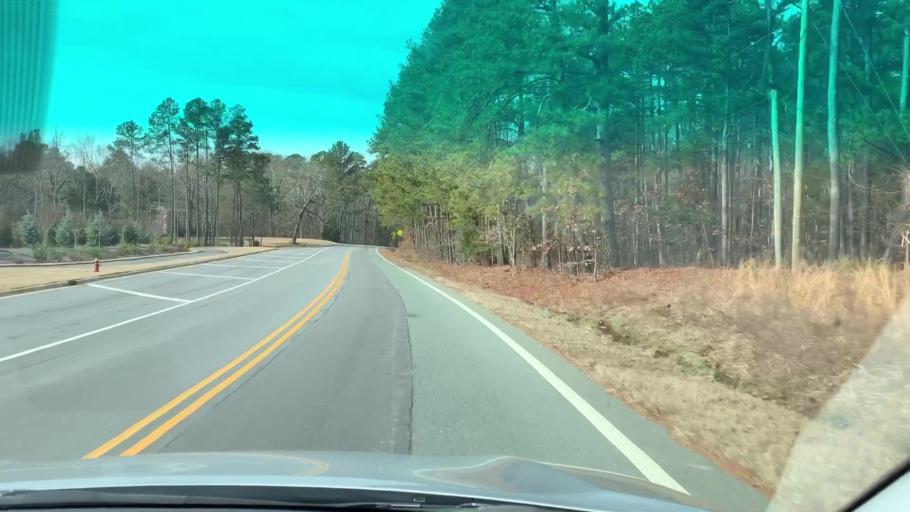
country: US
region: North Carolina
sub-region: Wake County
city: Green Level
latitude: 35.8459
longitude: -78.9198
